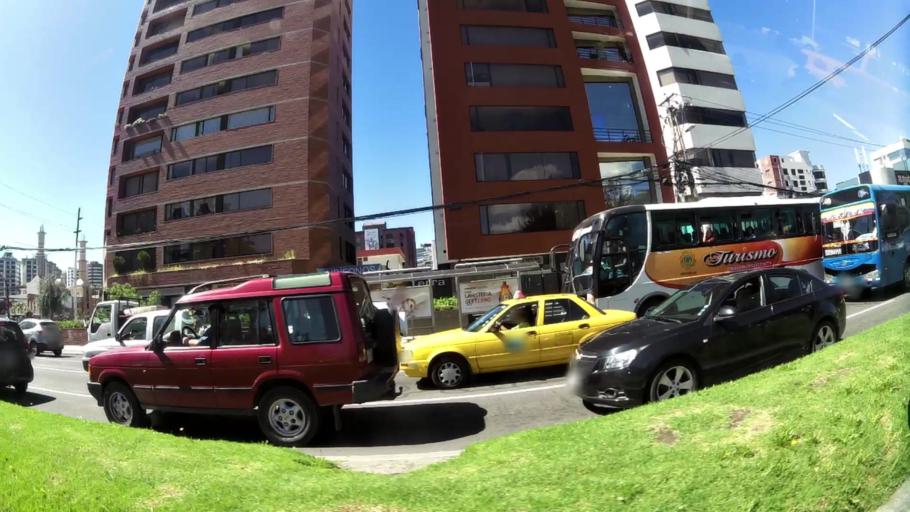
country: EC
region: Pichincha
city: Quito
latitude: -0.1892
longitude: -78.4831
